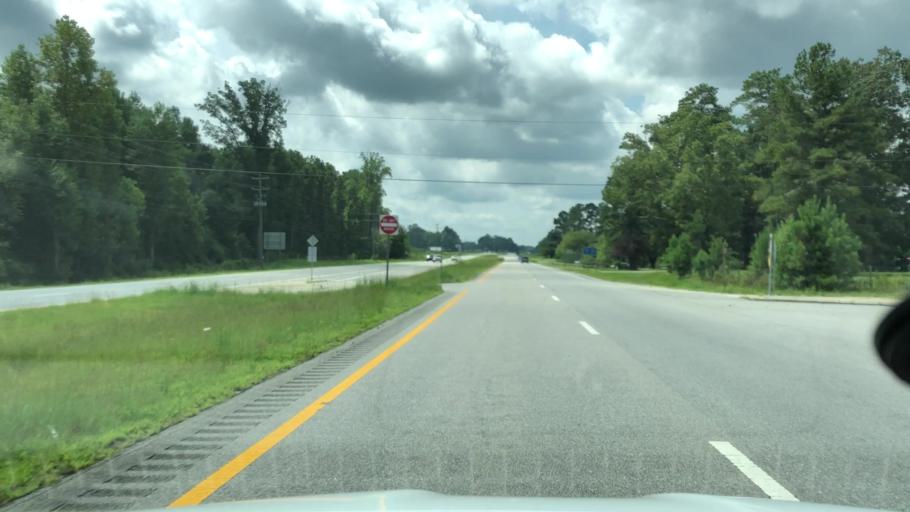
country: US
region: North Carolina
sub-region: Beaufort County
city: Washington
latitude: 35.4973
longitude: -77.1048
